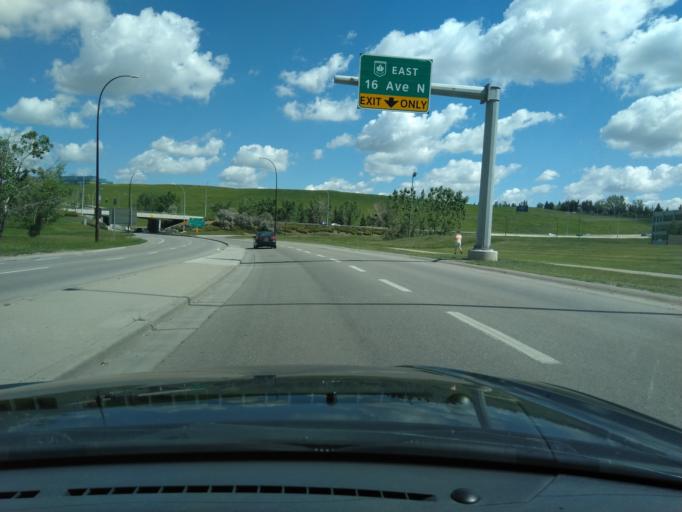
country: CA
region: Alberta
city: Calgary
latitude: 51.0644
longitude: -114.1481
